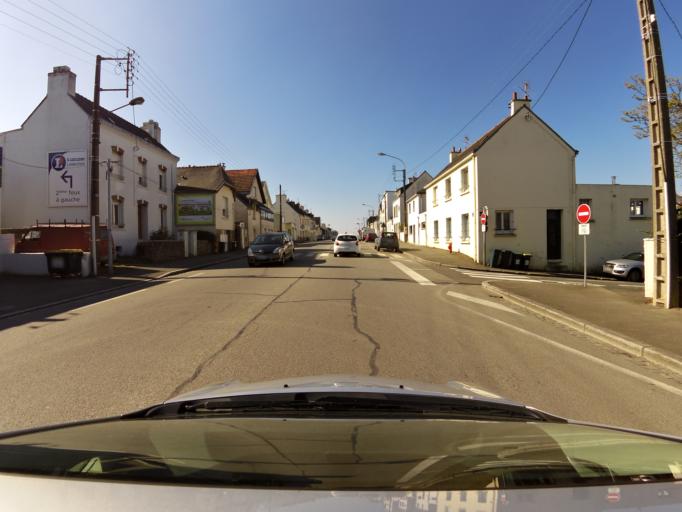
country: FR
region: Brittany
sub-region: Departement du Morbihan
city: Lanester
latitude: 47.7736
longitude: -3.3473
